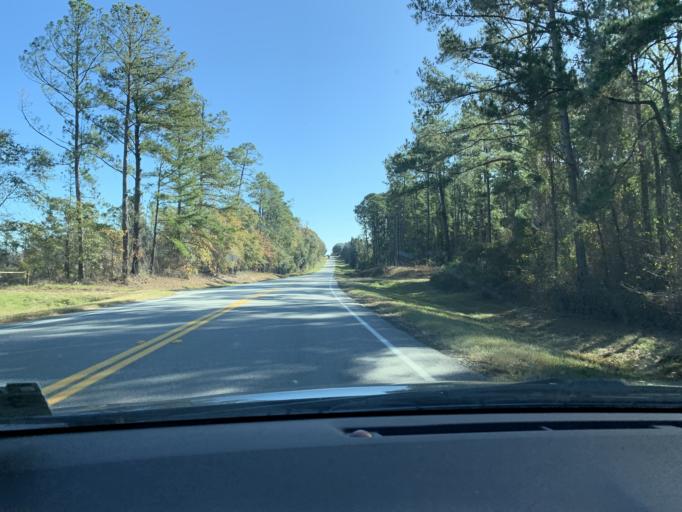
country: US
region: Georgia
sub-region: Ben Hill County
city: Fitzgerald
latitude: 31.7784
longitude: -83.0790
